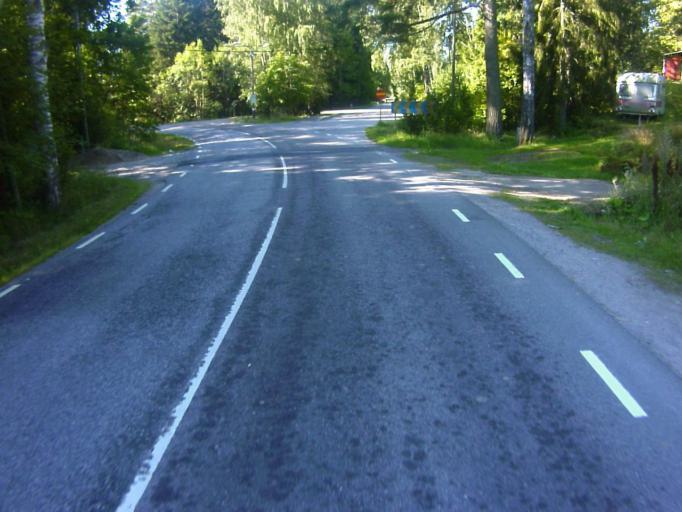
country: SE
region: Soedermanland
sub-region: Eskilstuna Kommun
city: Skogstorp
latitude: 59.3294
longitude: 16.4235
